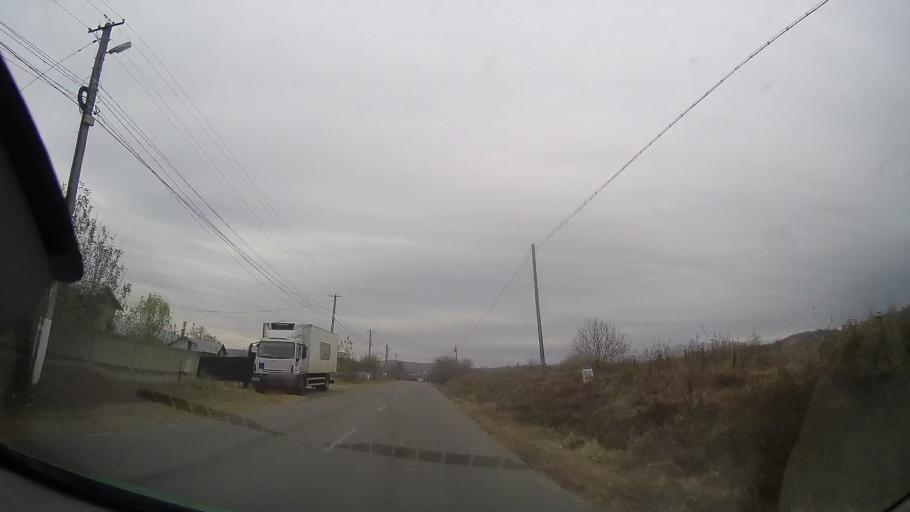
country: RO
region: Prahova
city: Mocesti
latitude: 45.0630
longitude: 26.2472
